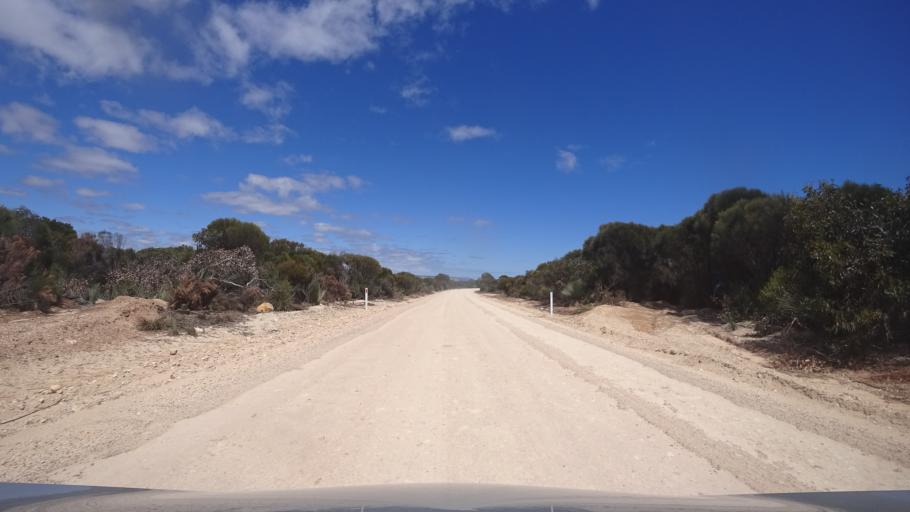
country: AU
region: South Australia
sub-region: Kangaroo Island
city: Kingscote
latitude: -35.6392
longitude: 137.2345
